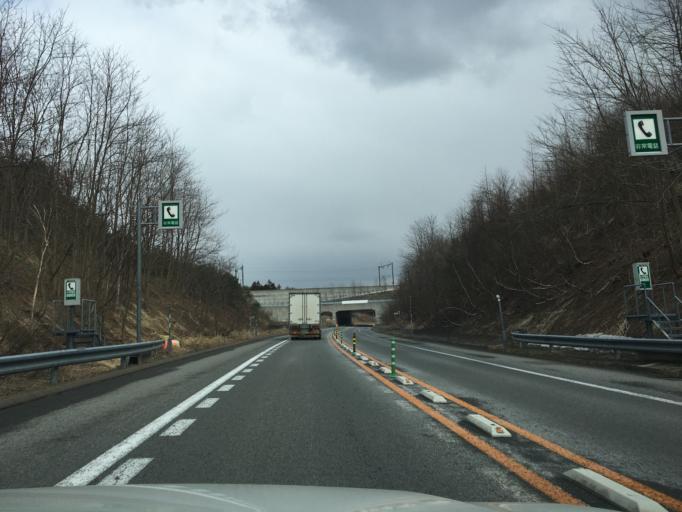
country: JP
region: Aomori
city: Aomori Shi
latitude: 40.8037
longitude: 140.6904
